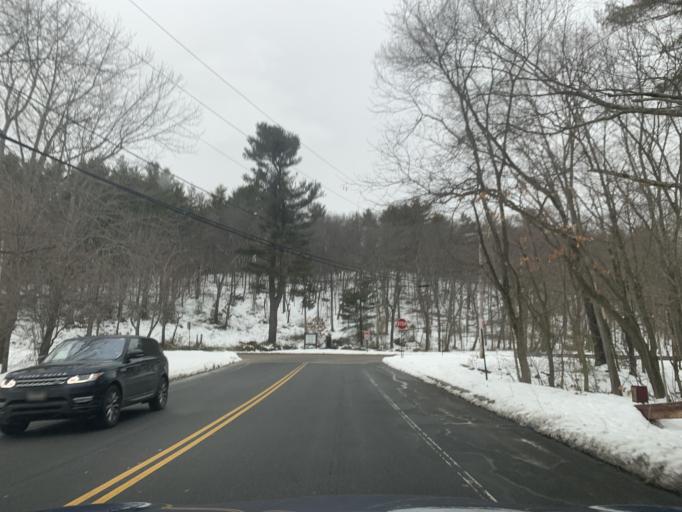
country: US
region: Massachusetts
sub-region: Norfolk County
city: Milton
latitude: 42.2085
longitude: -71.1020
